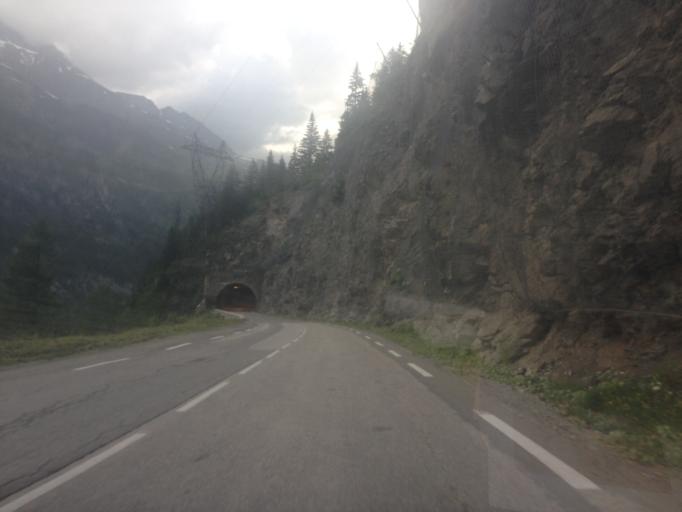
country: FR
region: Rhone-Alpes
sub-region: Departement de la Savoie
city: Tignes
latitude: 45.5043
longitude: 6.9294
